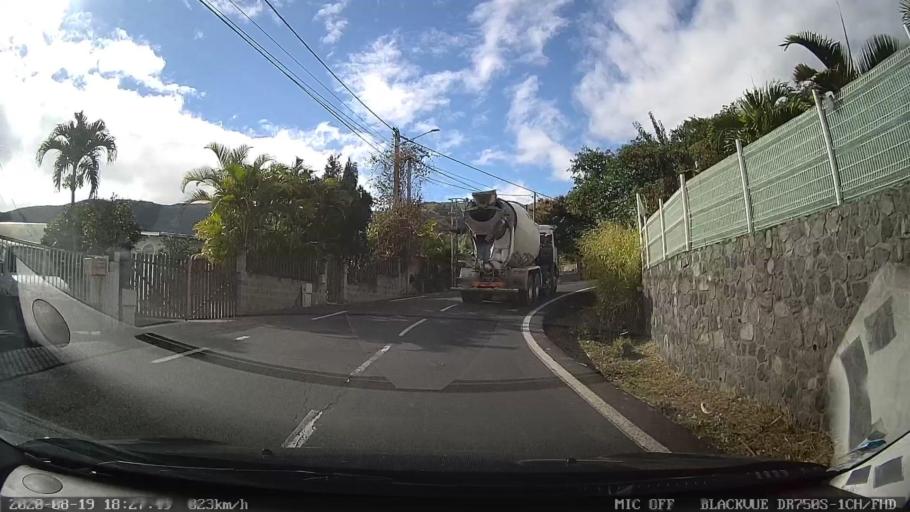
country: RE
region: Reunion
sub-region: Reunion
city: La Possession
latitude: -20.9559
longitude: 55.3511
